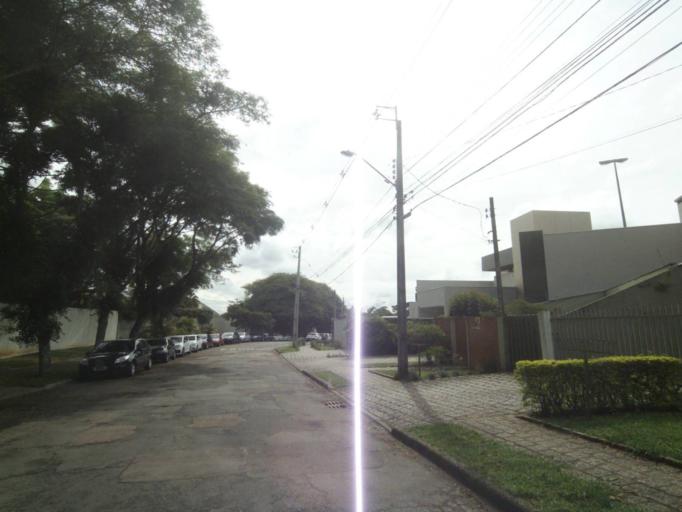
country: BR
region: Parana
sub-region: Curitiba
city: Curitiba
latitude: -25.4403
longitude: -49.3020
